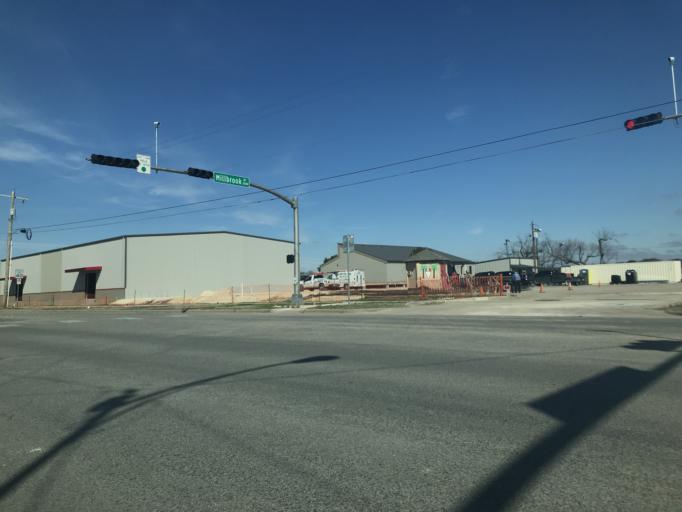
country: US
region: Texas
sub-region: Tom Green County
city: San Angelo
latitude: 31.4328
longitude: -100.4804
